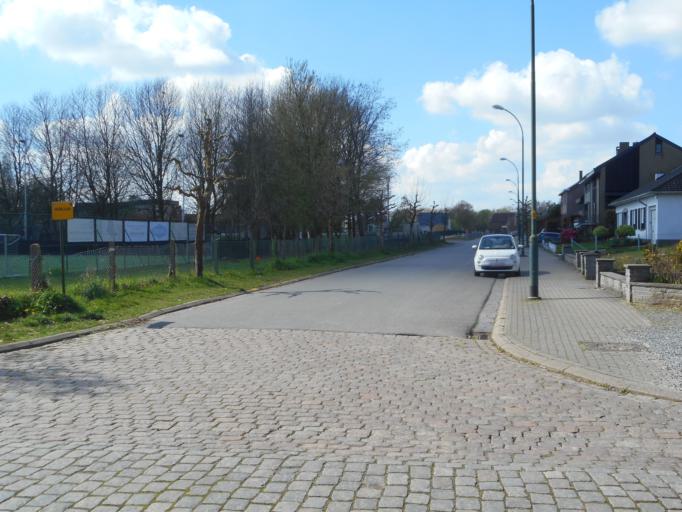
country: BE
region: Flanders
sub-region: Provincie Vlaams-Brabant
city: Grimbergen
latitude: 50.9557
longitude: 4.3653
